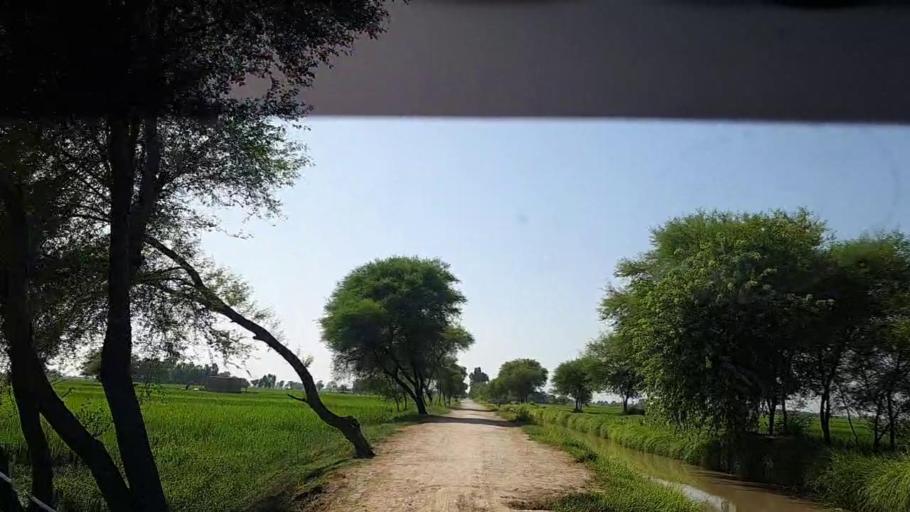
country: PK
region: Sindh
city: Ghauspur
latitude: 28.1764
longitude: 69.0441
